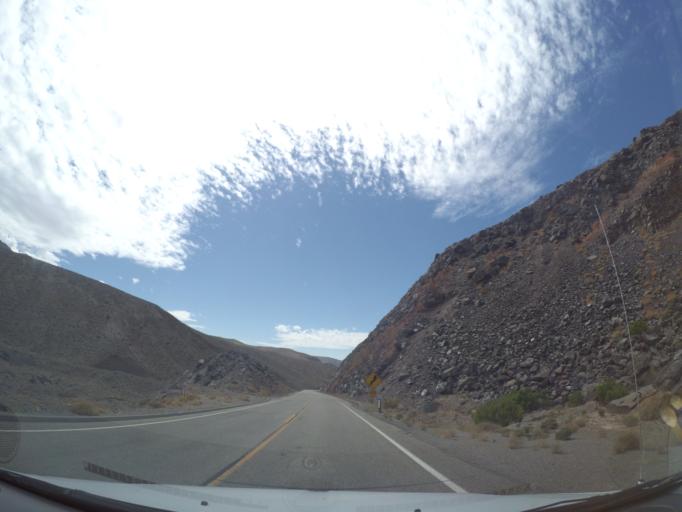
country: US
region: California
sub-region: San Bernardino County
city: Searles Valley
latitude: 36.3737
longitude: -117.2857
